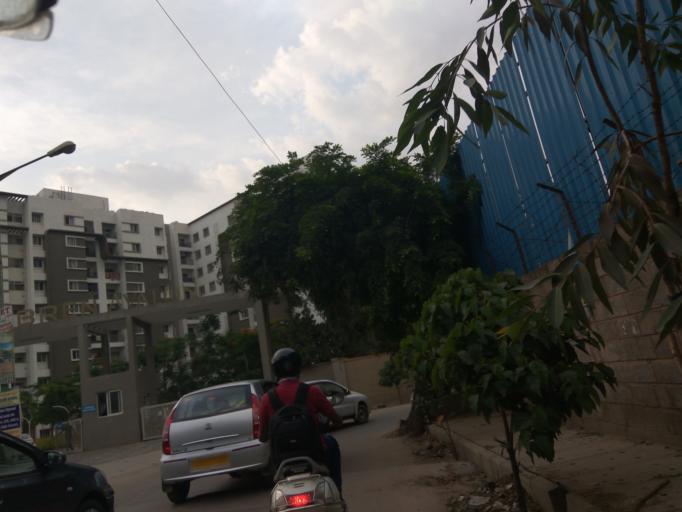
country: IN
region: Karnataka
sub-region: Bangalore Urban
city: Bangalore
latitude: 12.9751
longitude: 77.7069
